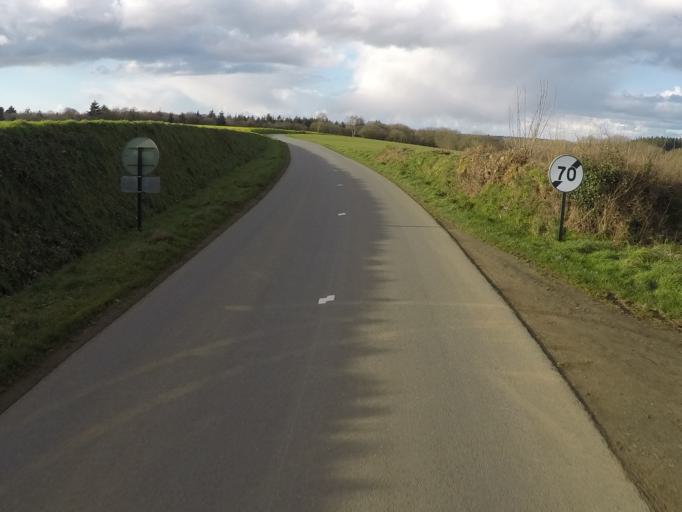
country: FR
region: Brittany
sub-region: Departement des Cotes-d'Armor
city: Goudelin
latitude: 48.5897
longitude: -2.9839
